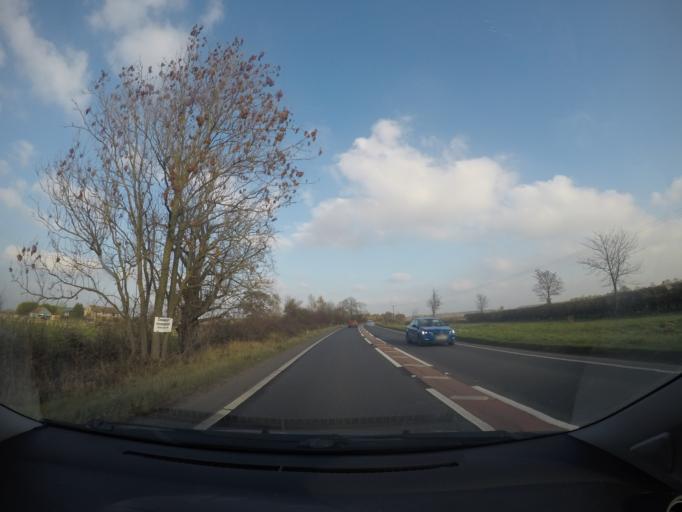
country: GB
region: England
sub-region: City of York
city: Murton
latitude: 54.0037
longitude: -1.0107
